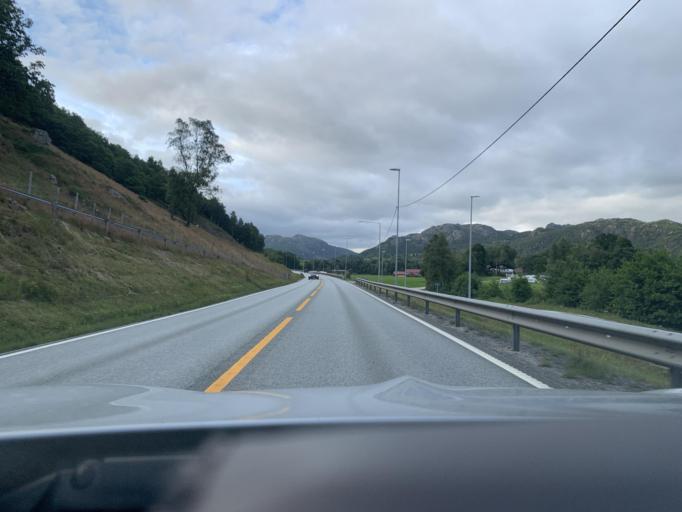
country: NO
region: Rogaland
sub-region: Bjerkreim
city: Vikesa
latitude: 58.5997
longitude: 6.0820
